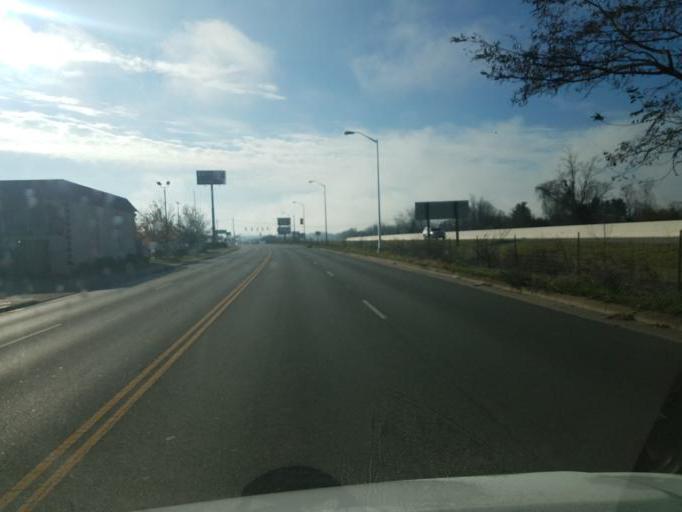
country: US
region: Ohio
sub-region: Scioto County
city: Wheelersburg
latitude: 38.7245
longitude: -82.8598
